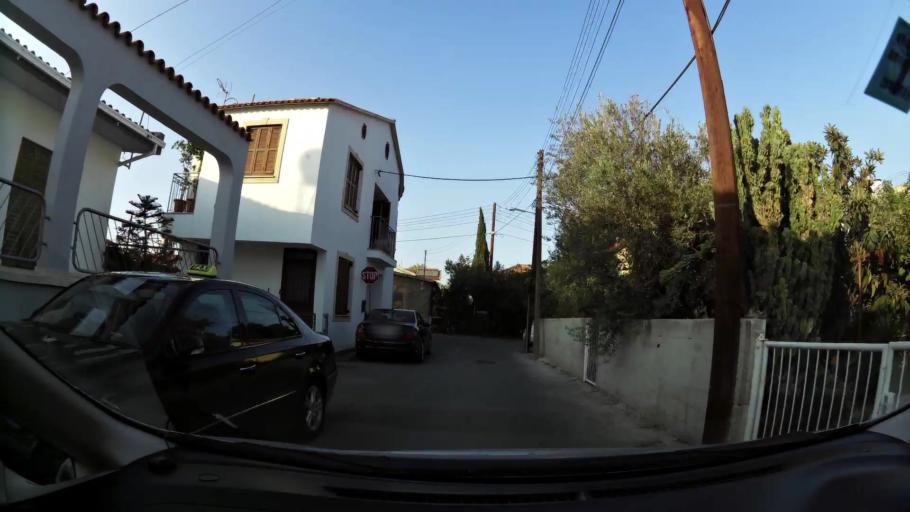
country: CY
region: Lefkosia
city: Nicosia
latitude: 35.1642
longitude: 33.3379
